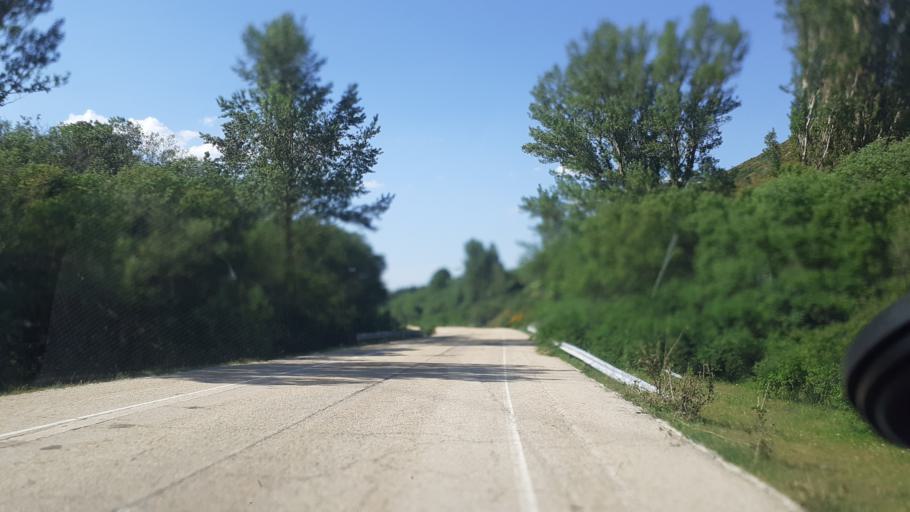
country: ES
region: Madrid
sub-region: Provincia de Madrid
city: Somosierra
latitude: 41.1528
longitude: -3.5823
